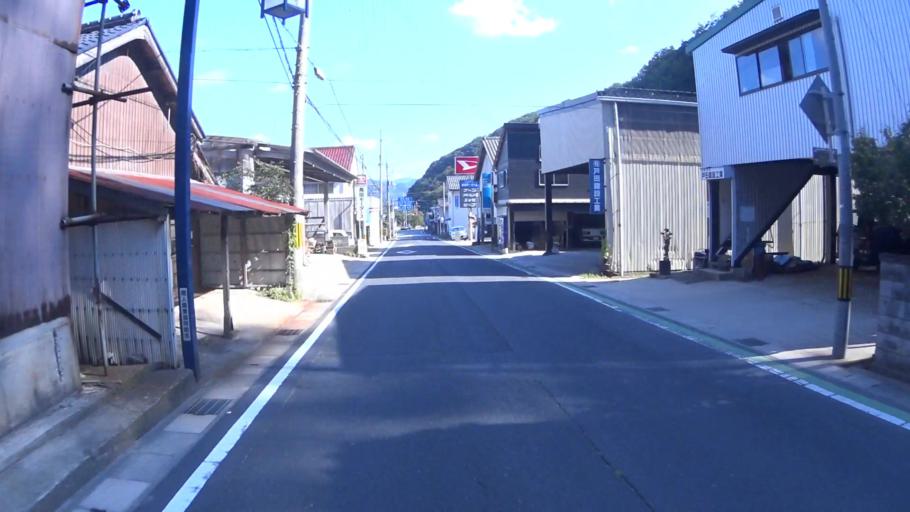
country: JP
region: Kyoto
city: Miyazu
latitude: 35.7325
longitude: 135.0944
